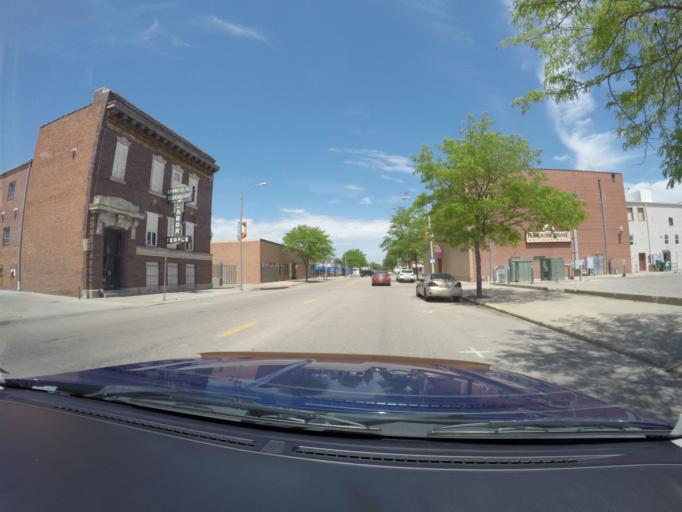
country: US
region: Nebraska
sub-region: Hall County
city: Grand Island
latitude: 40.9239
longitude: -98.3427
